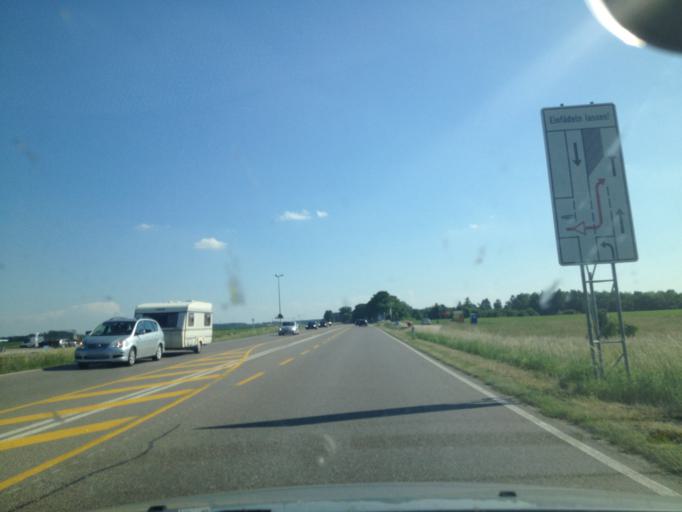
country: DE
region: Bavaria
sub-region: Swabia
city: Obergriesbach
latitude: 48.4149
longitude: 11.0892
